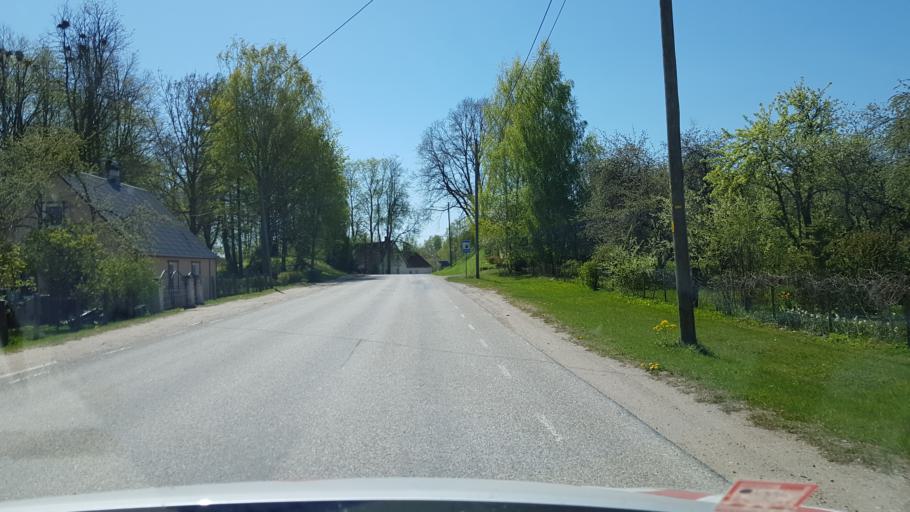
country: EE
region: Vorumaa
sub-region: Antsla vald
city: Vana-Antsla
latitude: 57.8312
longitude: 26.5355
